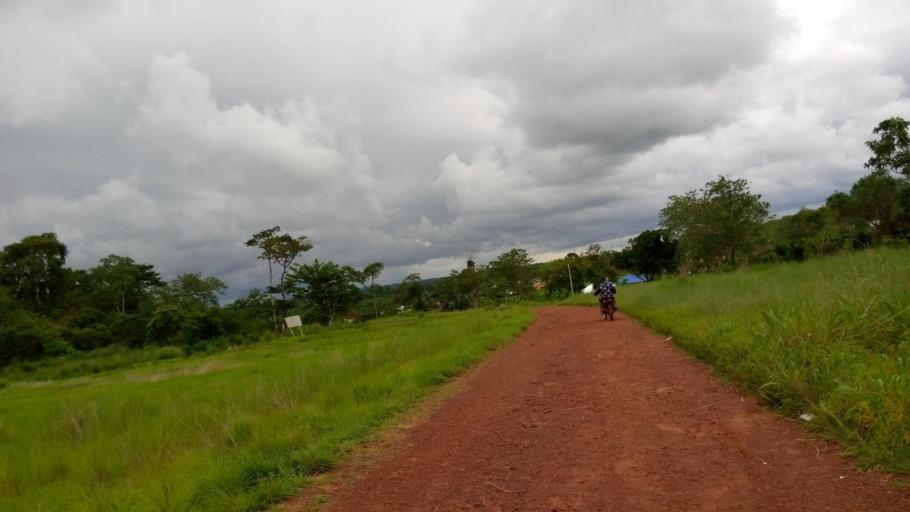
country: SL
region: Southern Province
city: Moyamba
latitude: 8.1622
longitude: -12.4518
